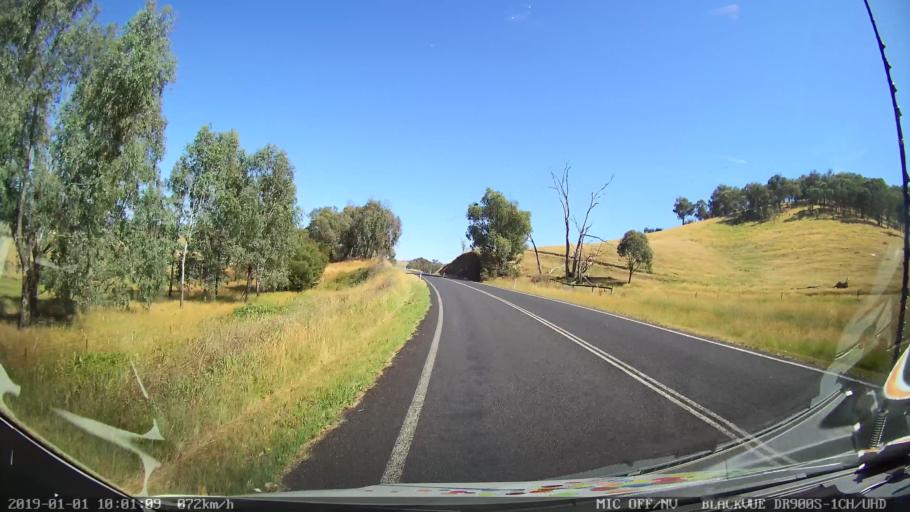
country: AU
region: New South Wales
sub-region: Snowy River
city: Jindabyne
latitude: -36.1944
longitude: 148.1027
